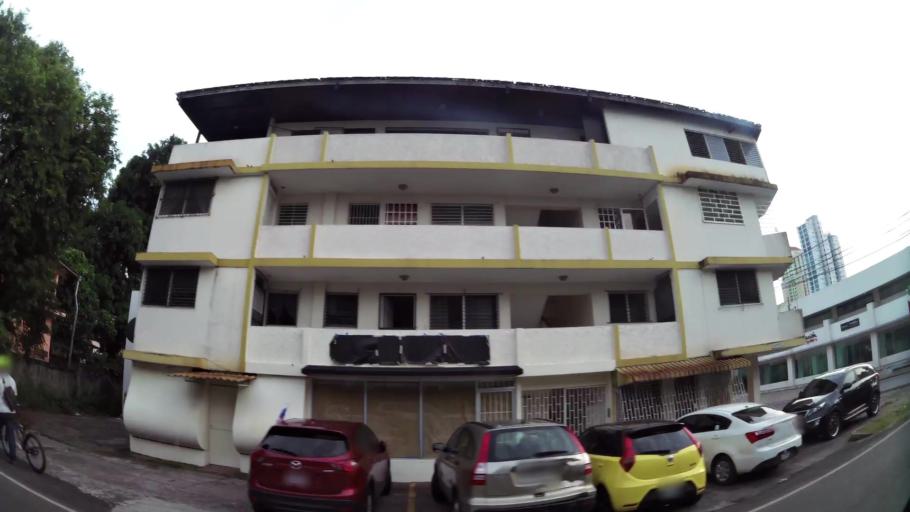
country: PA
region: Panama
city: Panama
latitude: 8.9940
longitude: -79.5094
